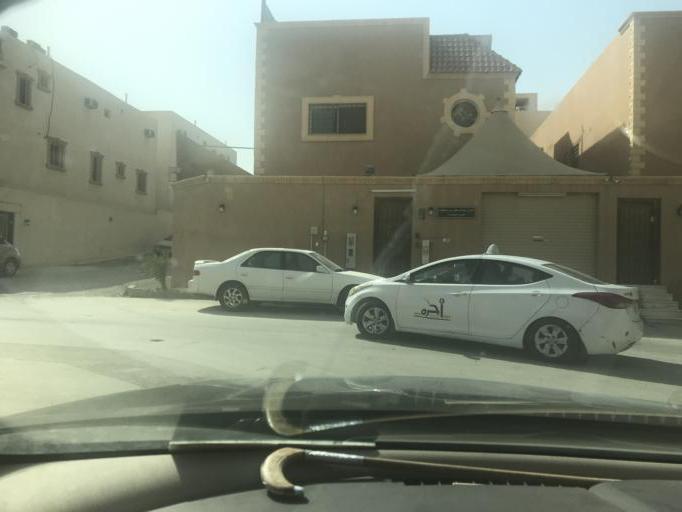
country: SA
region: Ar Riyad
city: Riyadh
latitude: 24.7479
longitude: 46.7652
